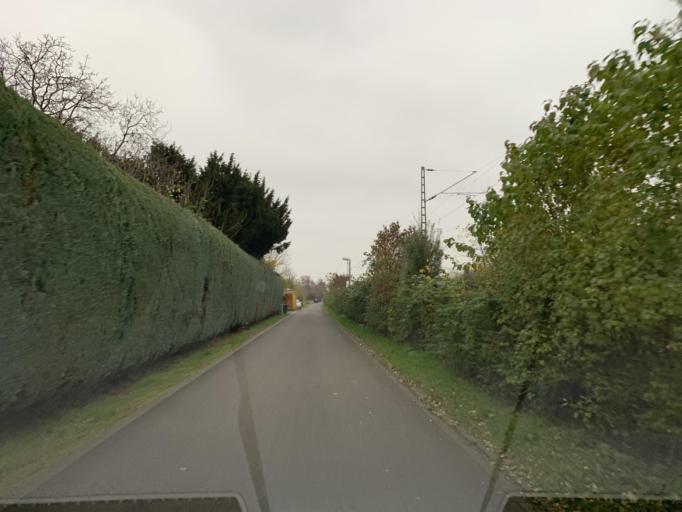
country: DE
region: North Rhine-Westphalia
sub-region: Regierungsbezirk Munster
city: Muenster
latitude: 51.9757
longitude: 7.6545
